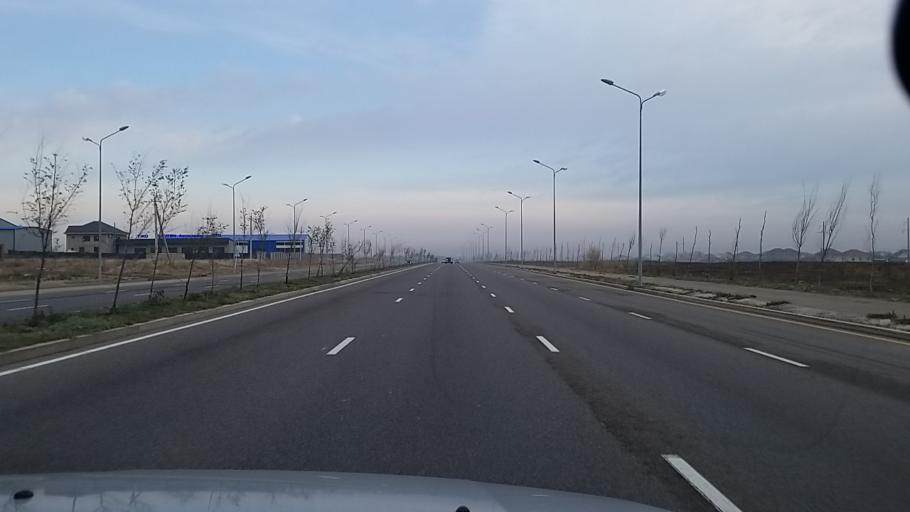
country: KZ
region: Almaty Oblysy
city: Burunday
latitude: 43.3376
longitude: 76.8335
